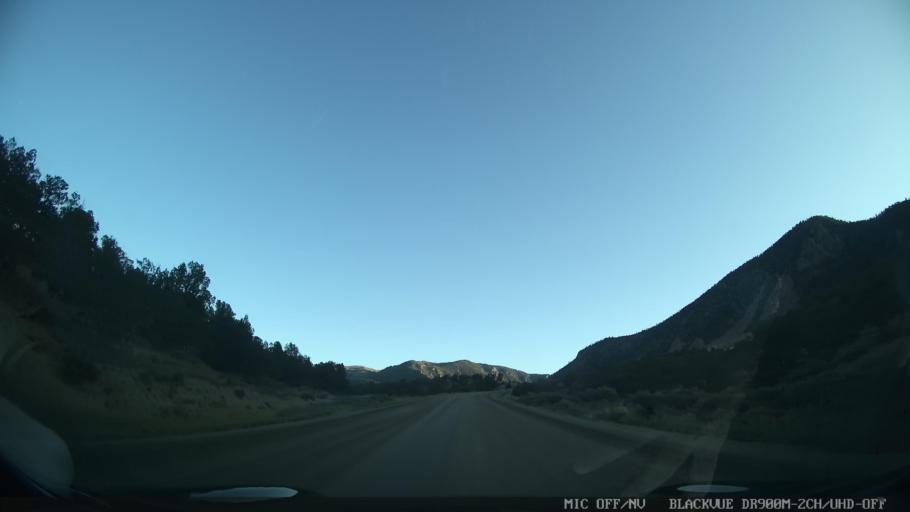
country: US
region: Colorado
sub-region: Grand County
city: Kremmling
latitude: 39.9816
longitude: -106.4968
